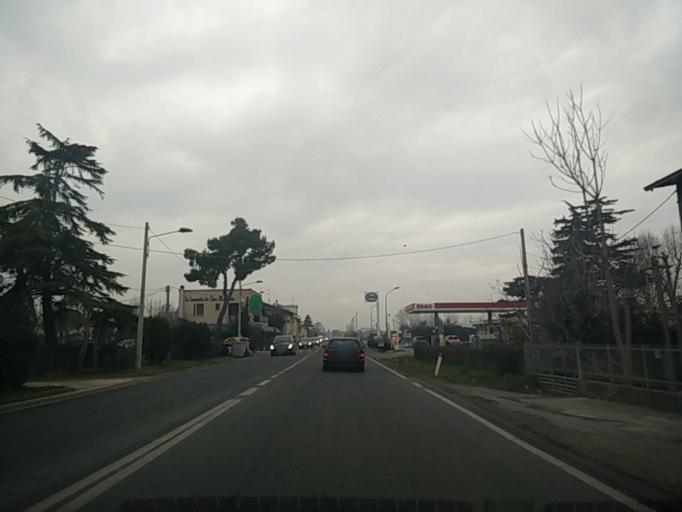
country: IT
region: Emilia-Romagna
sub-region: Provincia di Rimini
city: Santa Giustina
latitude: 44.0700
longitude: 12.5054
